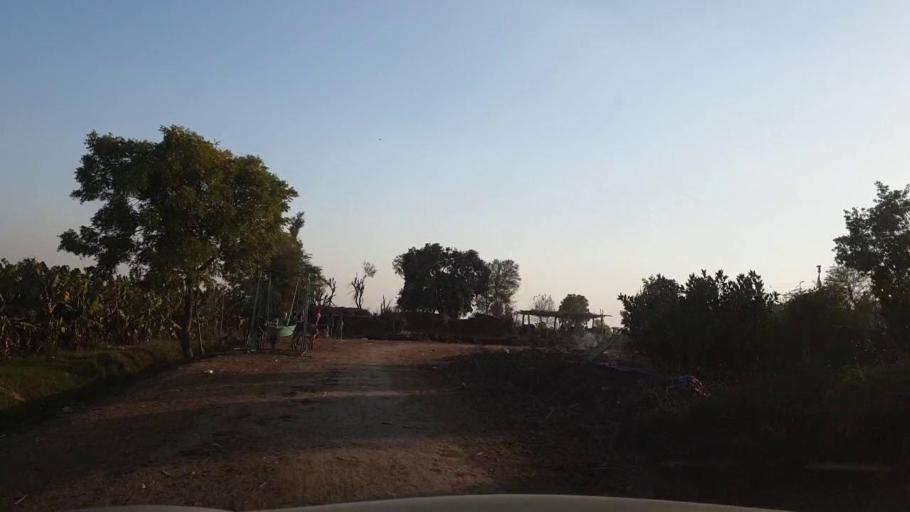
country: PK
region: Sindh
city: Tando Allahyar
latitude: 25.5878
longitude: 68.6982
